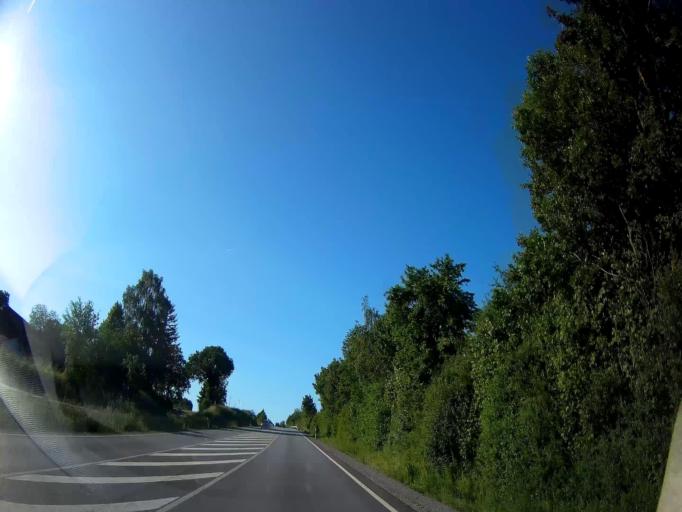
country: DE
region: Bavaria
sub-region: Lower Bavaria
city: Landau an der Isar
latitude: 48.6314
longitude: 12.7103
